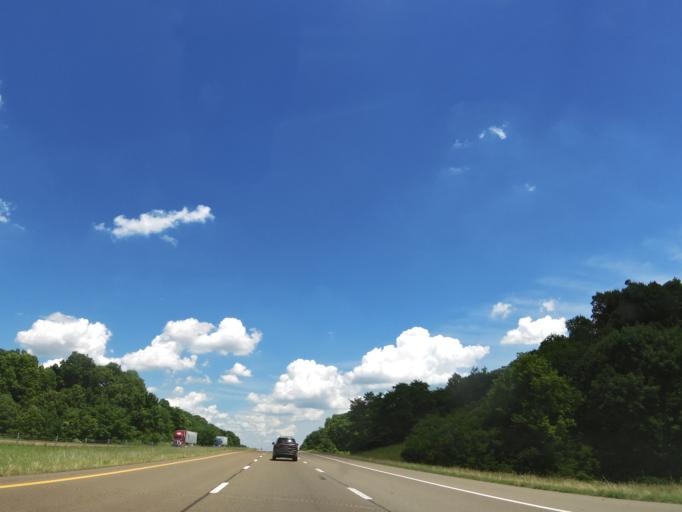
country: US
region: Tennessee
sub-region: Dyer County
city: Dyersburg
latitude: 36.0744
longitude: -89.4885
